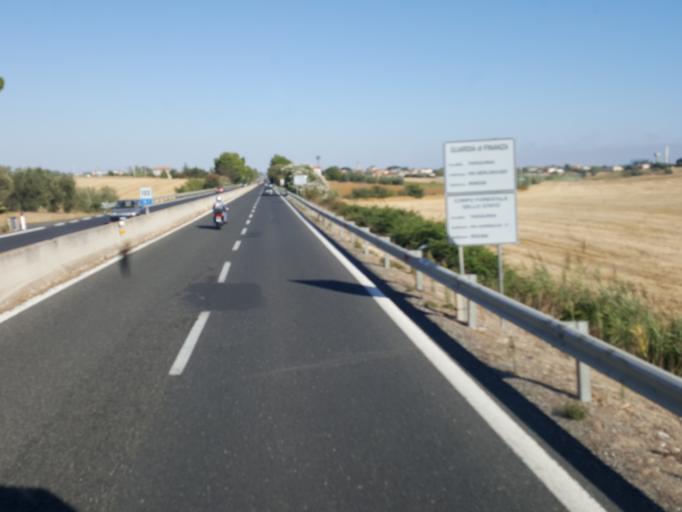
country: IT
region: Latium
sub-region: Provincia di Viterbo
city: Pescia Romana
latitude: 42.4069
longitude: 11.4833
